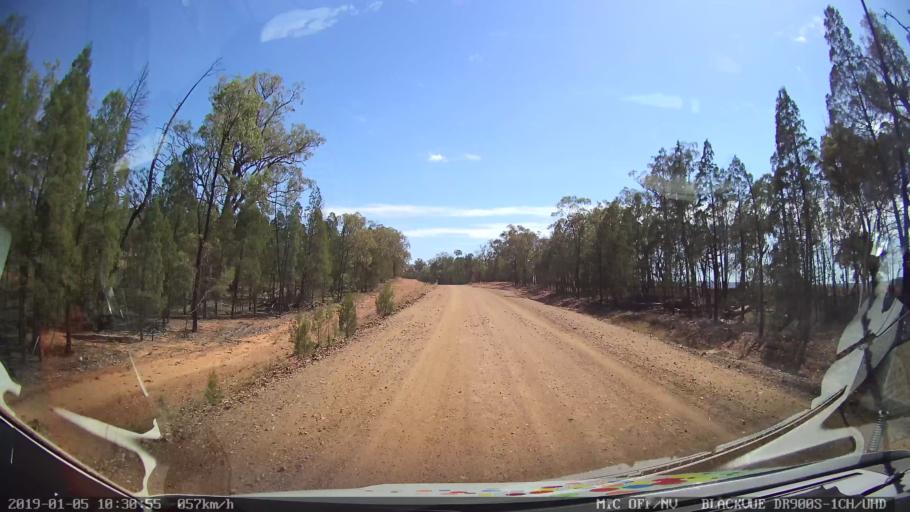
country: AU
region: New South Wales
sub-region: Gilgandra
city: Gilgandra
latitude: -31.5284
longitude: 148.9260
